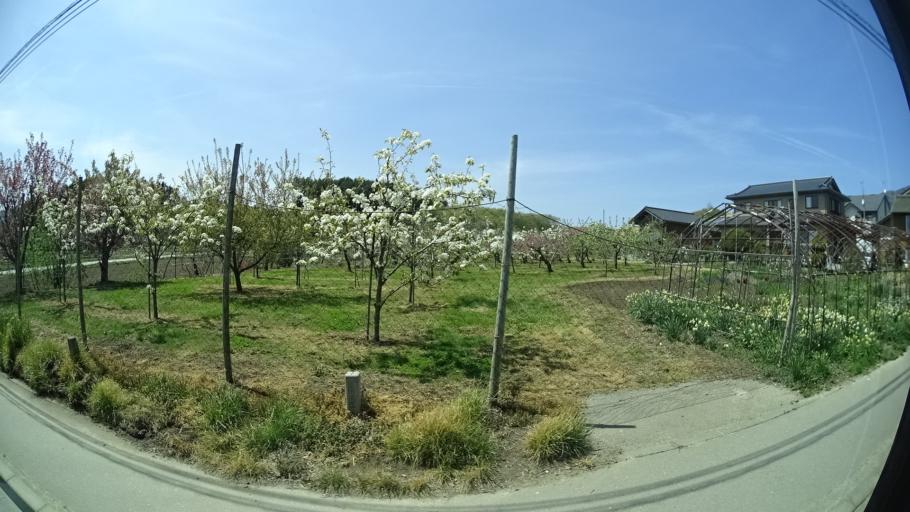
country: JP
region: Iwate
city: Ofunato
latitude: 39.0204
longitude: 141.6470
